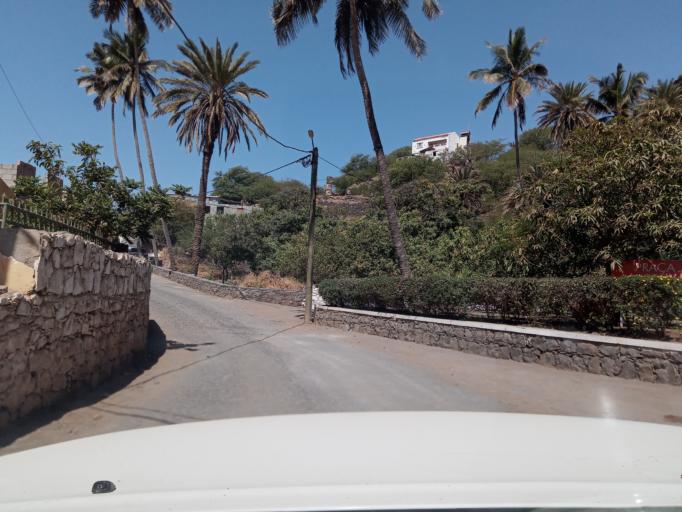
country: CV
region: Ribeira Grande de Santiago
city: Cidade Velha
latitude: 14.9153
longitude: -23.6054
